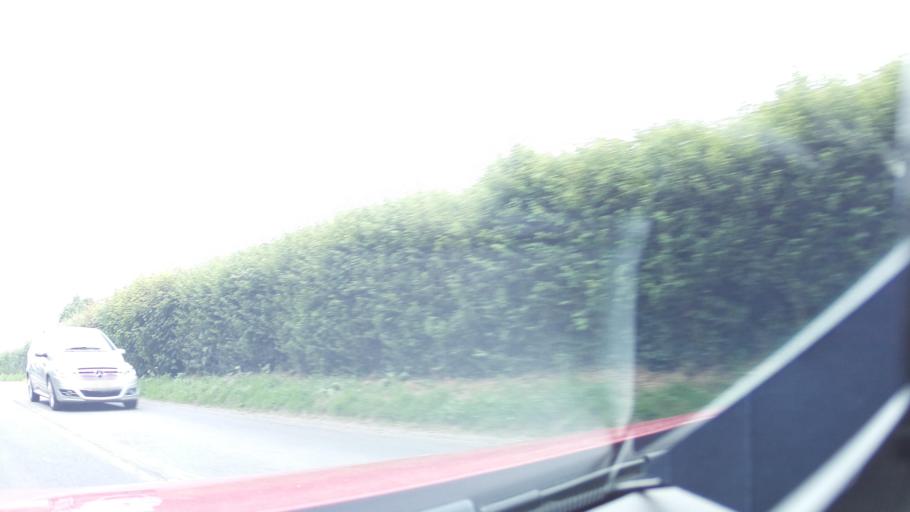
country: GB
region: England
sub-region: Somerset
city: Yeovil
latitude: 50.9219
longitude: -2.6792
